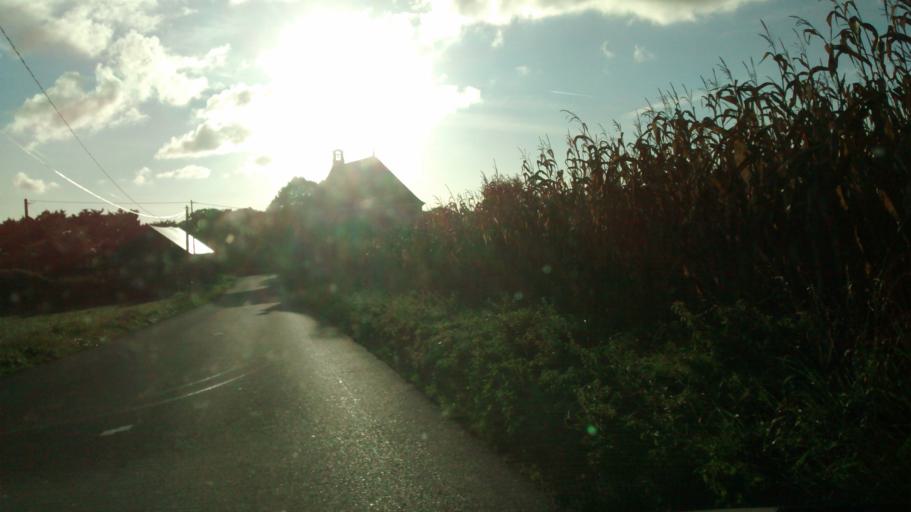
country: FR
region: Brittany
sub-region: Departement d'Ille-et-Vilaine
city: Saint-Meloir-des-Ondes
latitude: 48.6312
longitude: -1.8914
